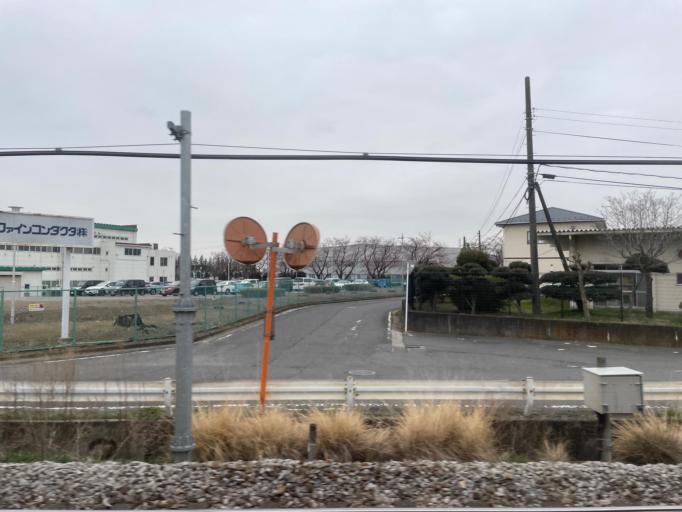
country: JP
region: Gunma
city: Maebashi-shi
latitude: 36.4085
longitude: 139.0348
